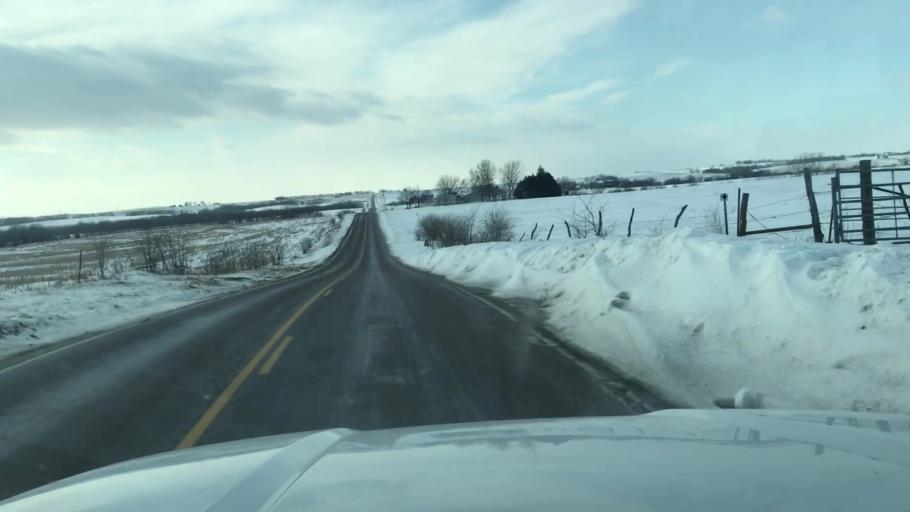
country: US
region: Missouri
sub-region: Nodaway County
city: Maryville
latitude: 40.2005
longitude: -94.8776
